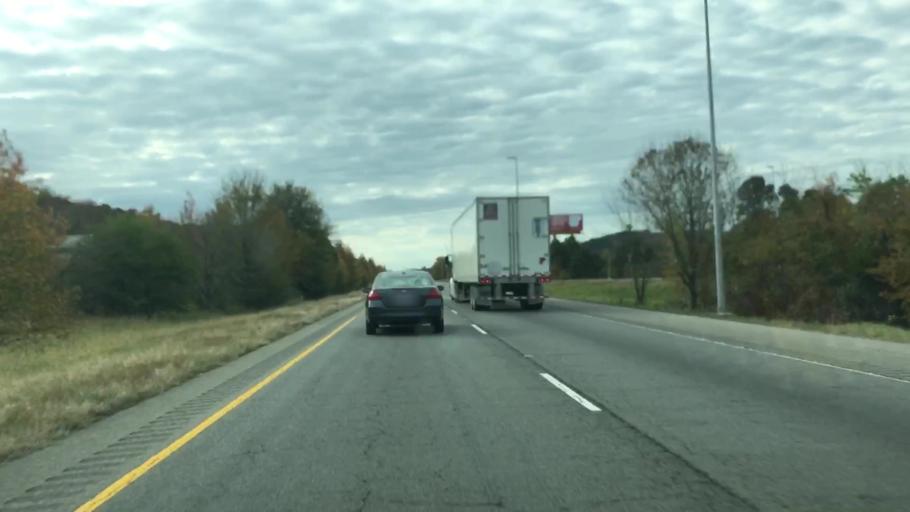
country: US
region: Arkansas
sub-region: Faulkner County
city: Conway
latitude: 35.1194
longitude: -92.4630
